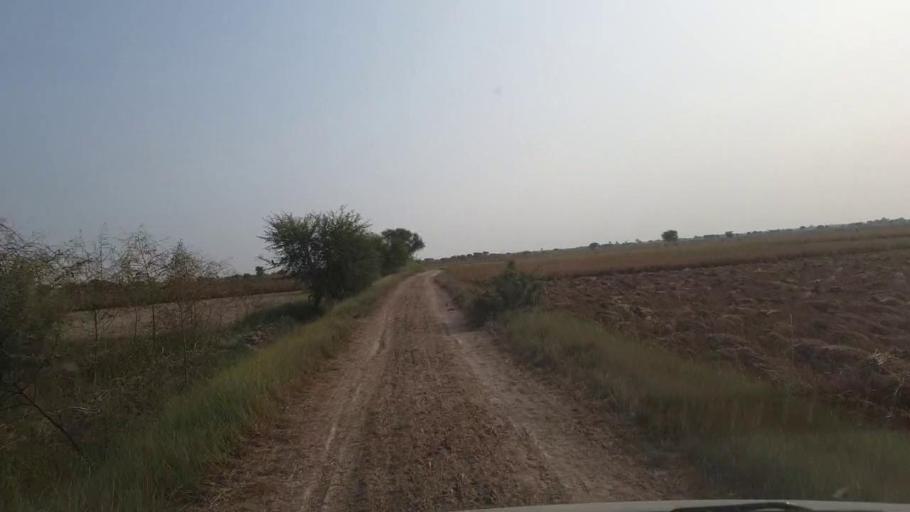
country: PK
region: Sindh
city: Matli
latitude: 25.0409
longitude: 68.7492
